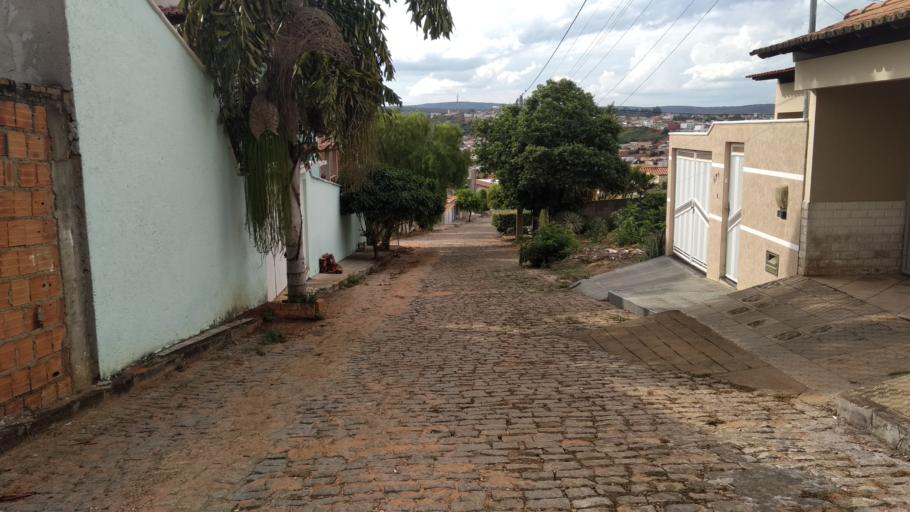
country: BR
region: Bahia
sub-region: Caetite
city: Caetite
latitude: -14.0727
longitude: -42.4788
